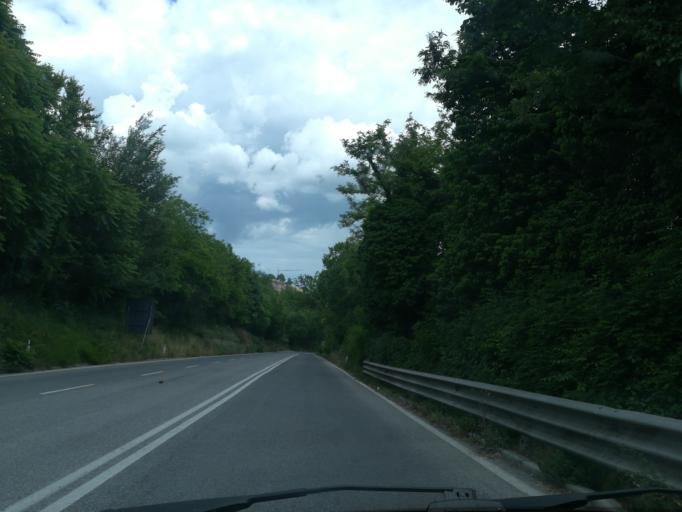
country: IT
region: The Marches
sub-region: Provincia di Macerata
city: Piediripa
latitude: 43.2838
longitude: 13.4724
